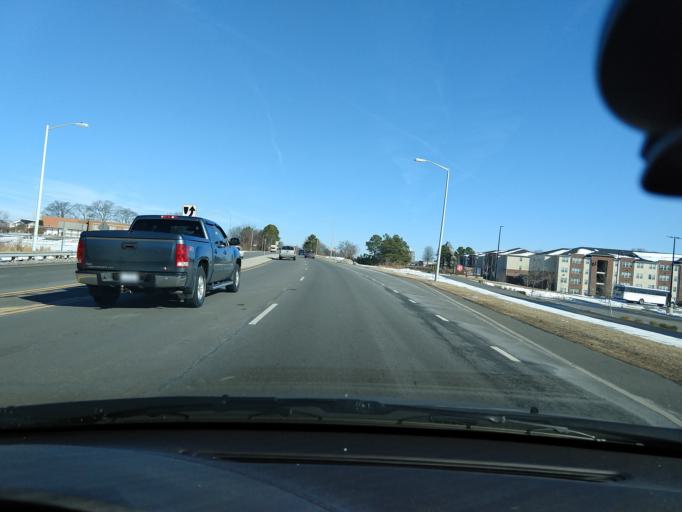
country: US
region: North Carolina
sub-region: Guilford County
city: Greensboro
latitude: 36.0603
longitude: -79.8006
